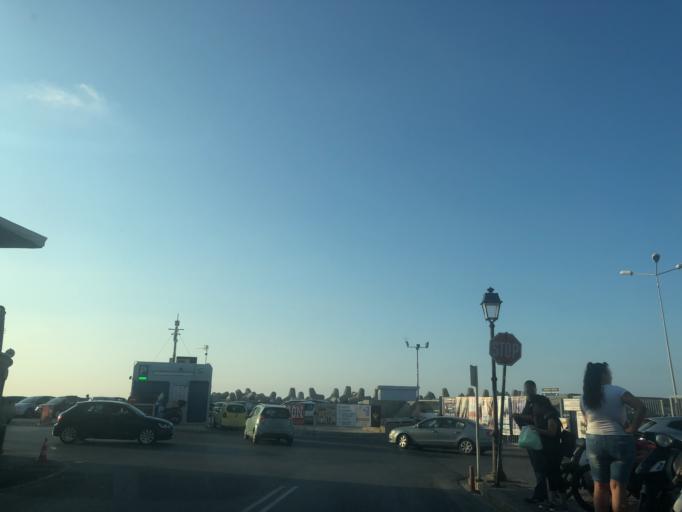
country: GR
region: Crete
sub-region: Nomos Rethymnis
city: Rethymno
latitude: 35.3710
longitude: 24.4760
